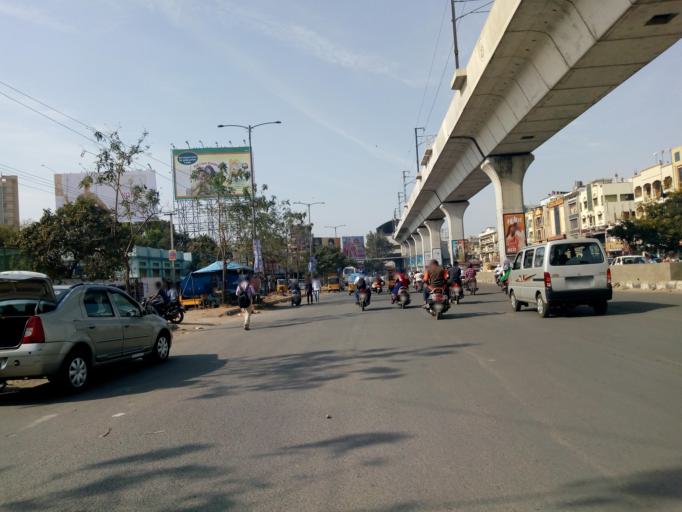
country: IN
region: Telangana
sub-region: Rangareddi
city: Lal Bahadur Nagar
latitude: 17.3476
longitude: 78.5496
